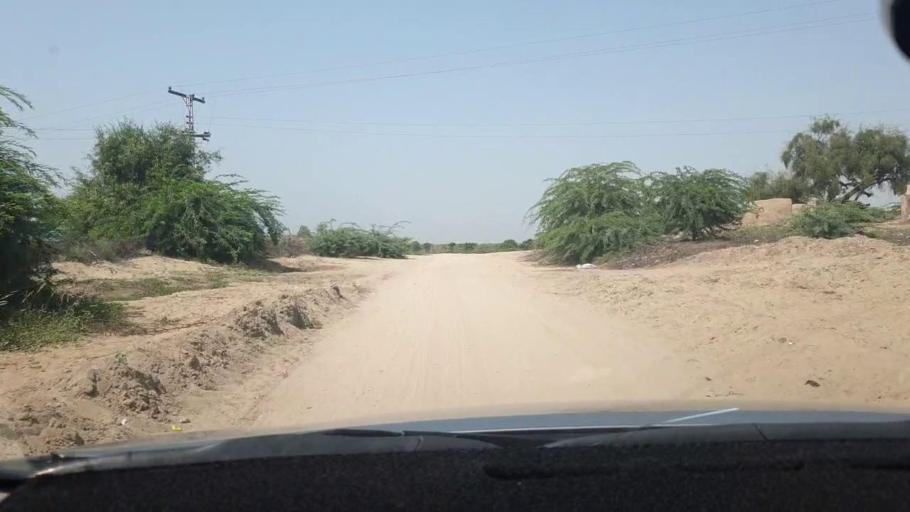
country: PK
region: Sindh
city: Tando Mittha Khan
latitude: 25.8452
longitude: 69.4254
